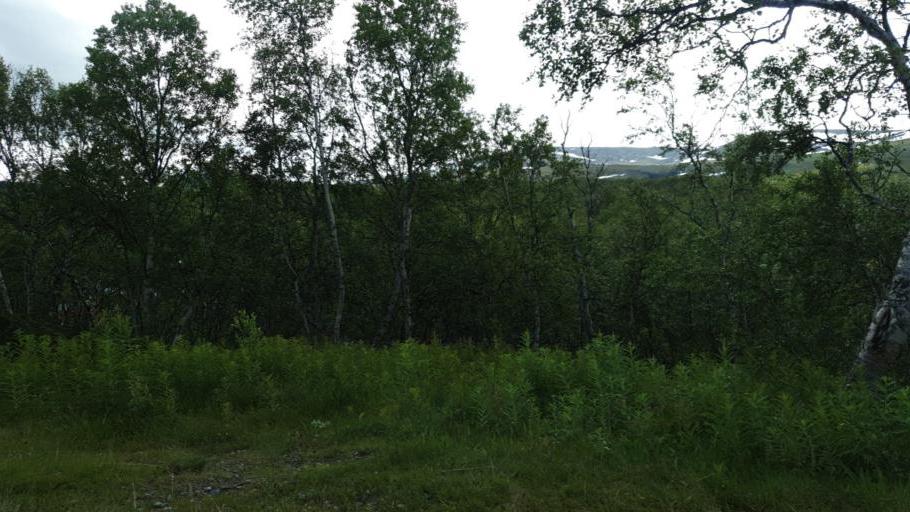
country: NO
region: Oppland
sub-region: Oystre Slidre
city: Heggenes
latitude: 61.4881
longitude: 8.8417
